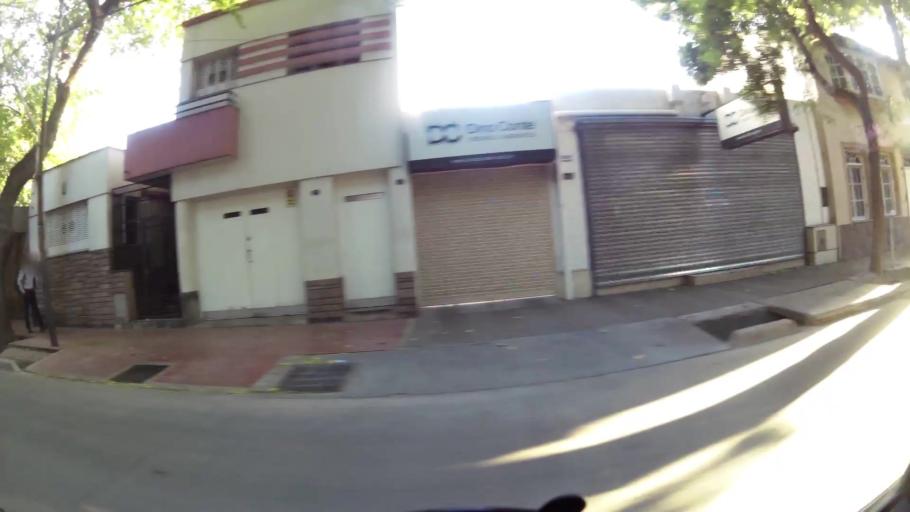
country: AR
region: Mendoza
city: Mendoza
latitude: -32.8793
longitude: -68.8438
